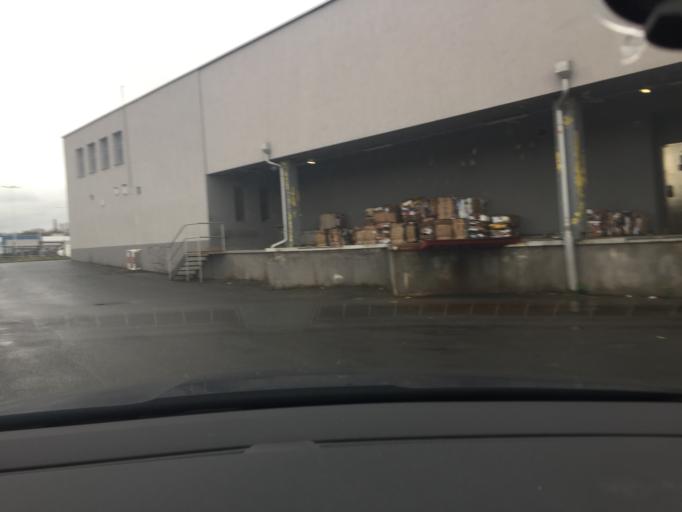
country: SK
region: Presovsky
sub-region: Okres Poprad
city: Poprad
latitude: 49.0596
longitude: 20.2895
